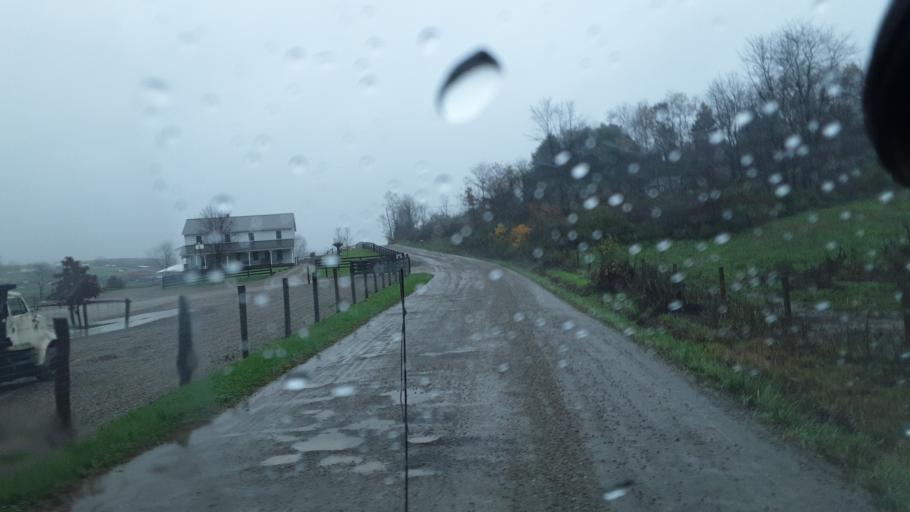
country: US
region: Ohio
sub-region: Vinton County
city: McArthur
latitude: 39.2265
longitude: -82.4766
